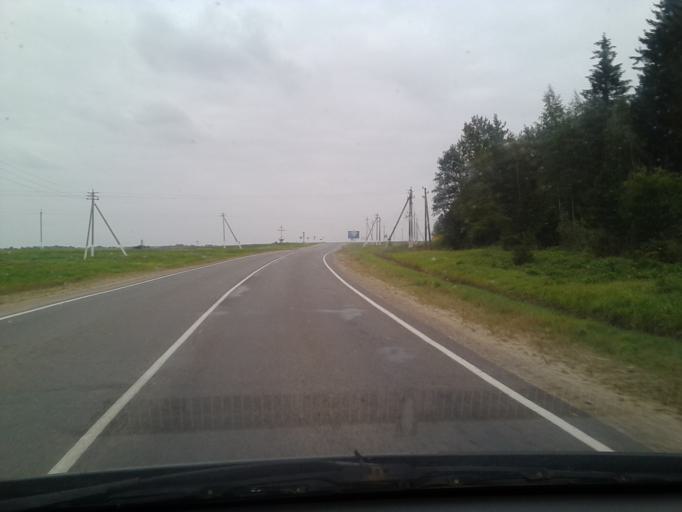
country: BY
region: Vitebsk
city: Pastavy
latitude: 55.1029
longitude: 26.8709
